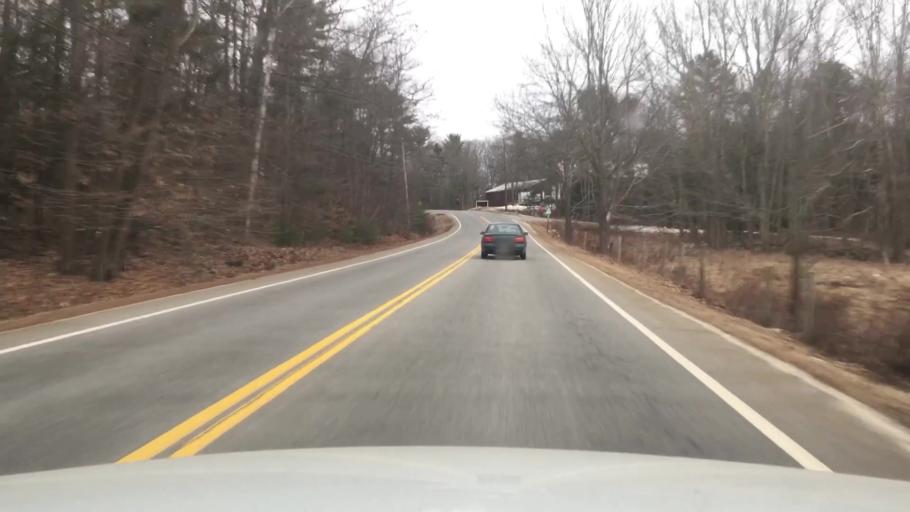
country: US
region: Maine
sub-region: Cumberland County
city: Freeport
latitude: 43.8826
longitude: -70.0368
